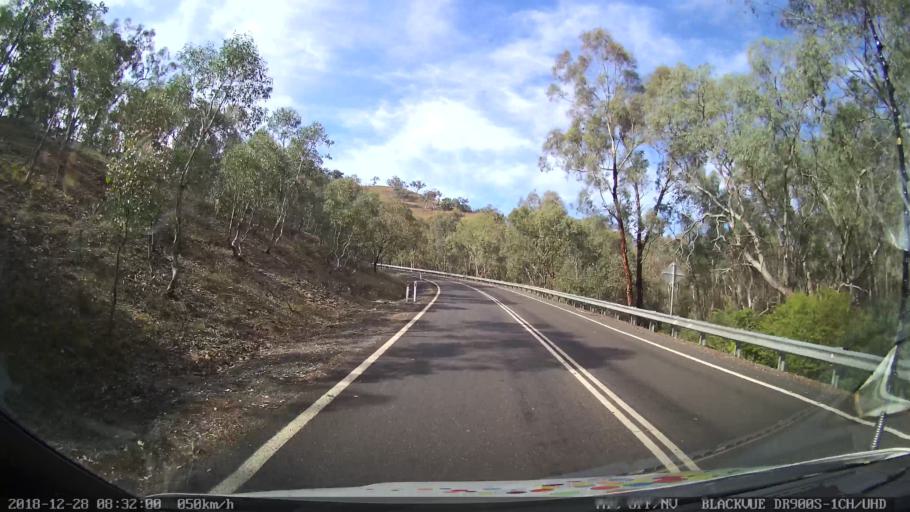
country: AU
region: New South Wales
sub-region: Blayney
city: Blayney
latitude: -33.9619
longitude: 149.3151
